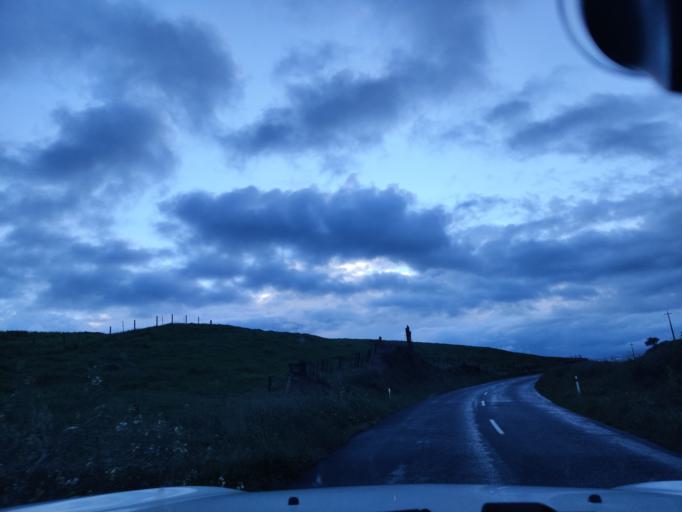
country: NZ
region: Waikato
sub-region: South Waikato District
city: Tokoroa
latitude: -38.1819
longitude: 175.7847
